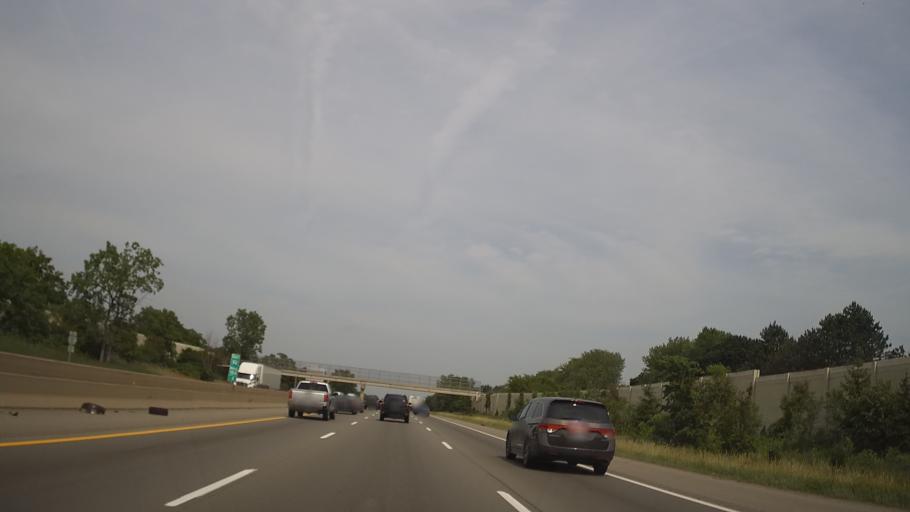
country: US
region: Michigan
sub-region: Washtenaw County
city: Ypsilanti
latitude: 42.2315
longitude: -83.5937
